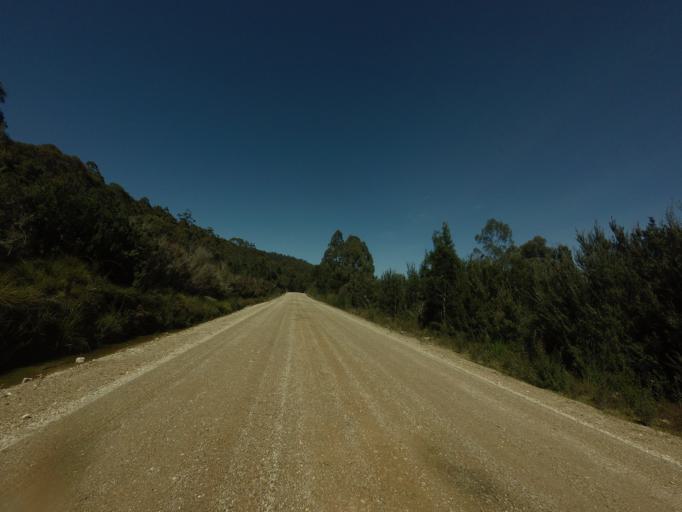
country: AU
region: Tasmania
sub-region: Huon Valley
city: Geeveston
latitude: -42.9935
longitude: 146.3715
